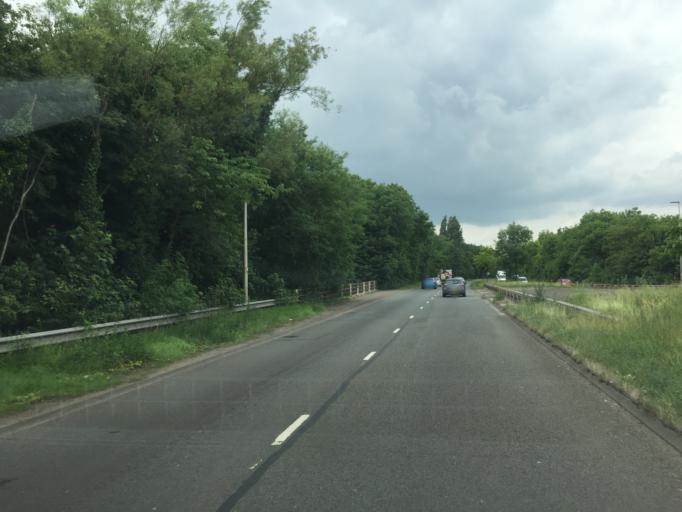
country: GB
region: England
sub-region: Sandwell
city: Smethwick
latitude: 52.5134
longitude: -1.9781
